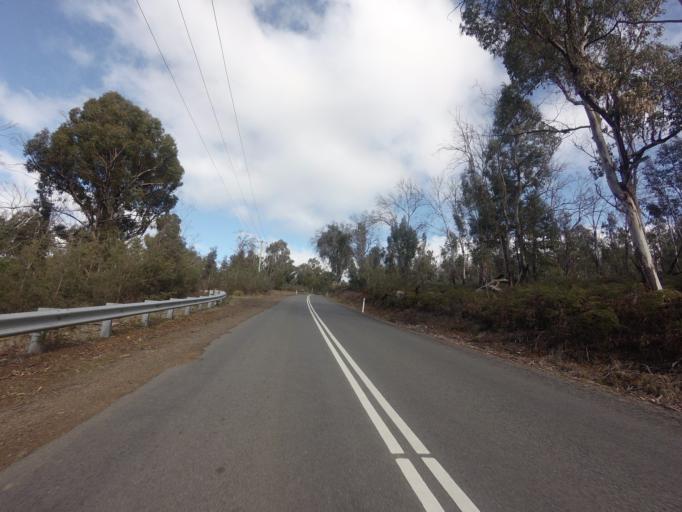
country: AU
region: Tasmania
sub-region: Derwent Valley
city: New Norfolk
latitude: -42.5498
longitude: 146.7145
